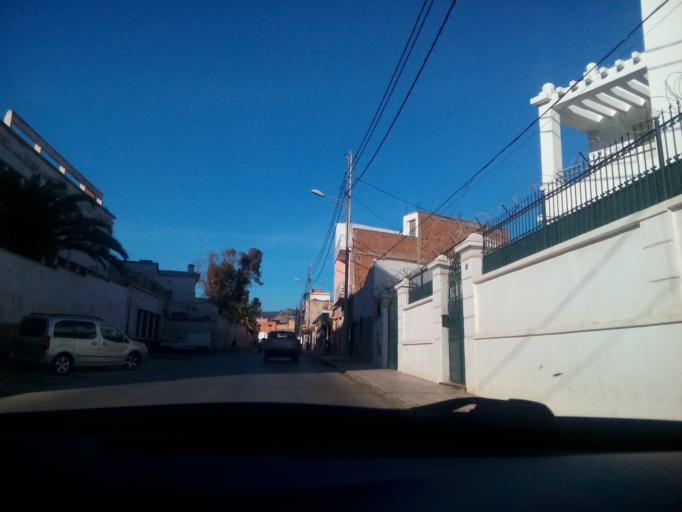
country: DZ
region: Oran
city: Oran
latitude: 35.6877
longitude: -0.6630
